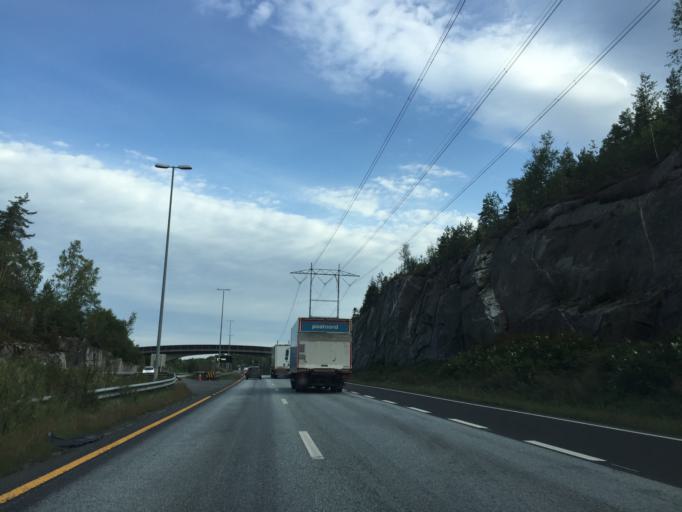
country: NO
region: Akershus
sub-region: Oppegard
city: Kolbotn
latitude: 59.8054
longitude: 10.8424
